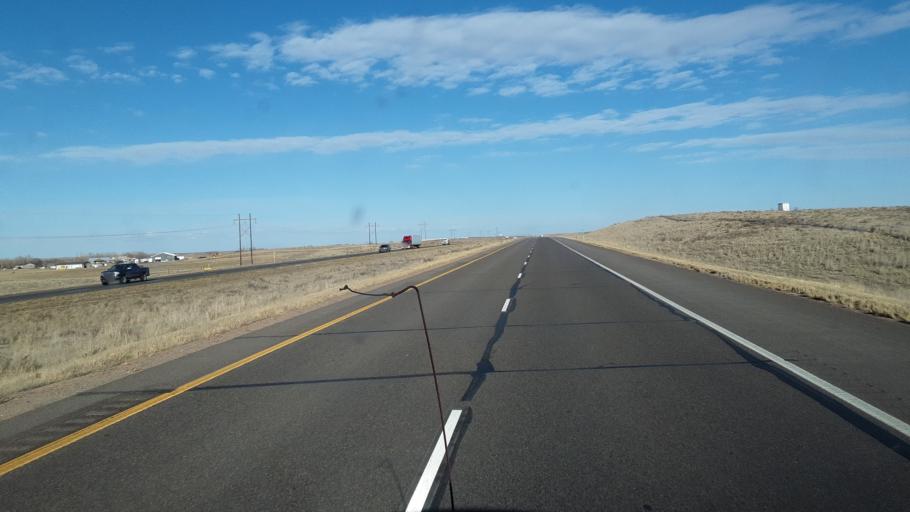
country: US
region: Colorado
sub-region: Morgan County
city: Brush
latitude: 40.3147
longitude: -103.5042
